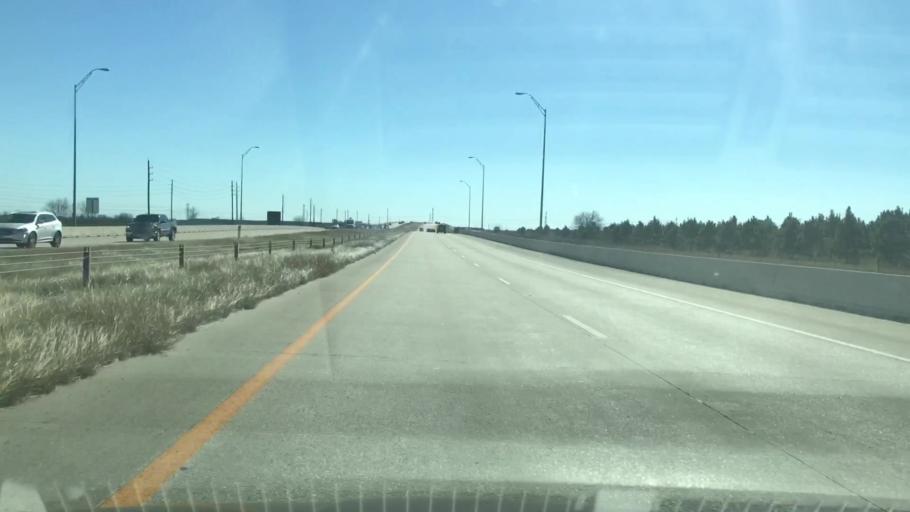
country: US
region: Texas
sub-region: Harris County
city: Cypress
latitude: 29.9288
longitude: -95.7630
